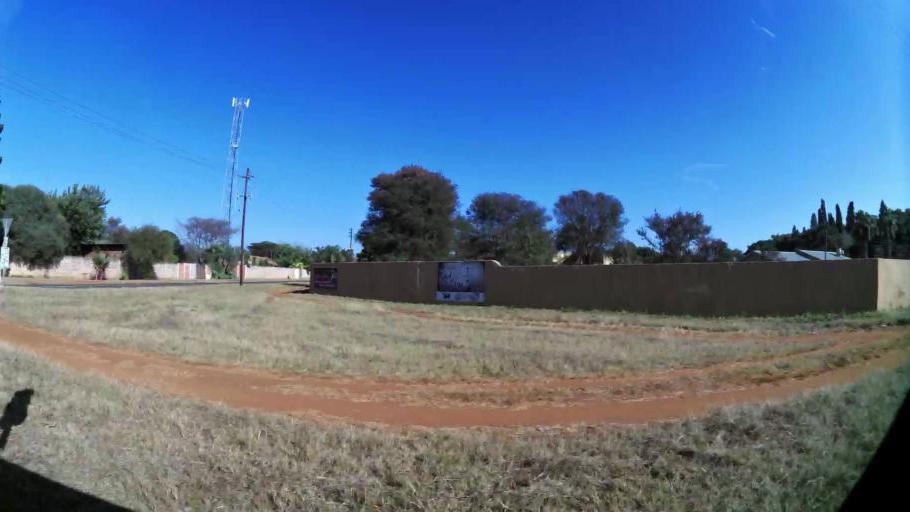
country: ZA
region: Gauteng
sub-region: City of Tshwane Metropolitan Municipality
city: Pretoria
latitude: -25.6555
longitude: 28.1312
